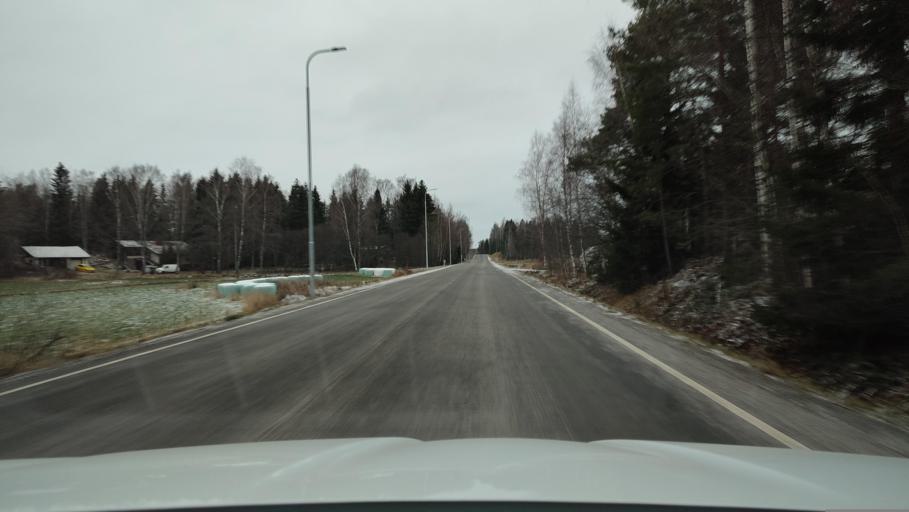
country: FI
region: Ostrobothnia
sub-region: Vaasa
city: Ristinummi
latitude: 63.0419
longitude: 21.7788
